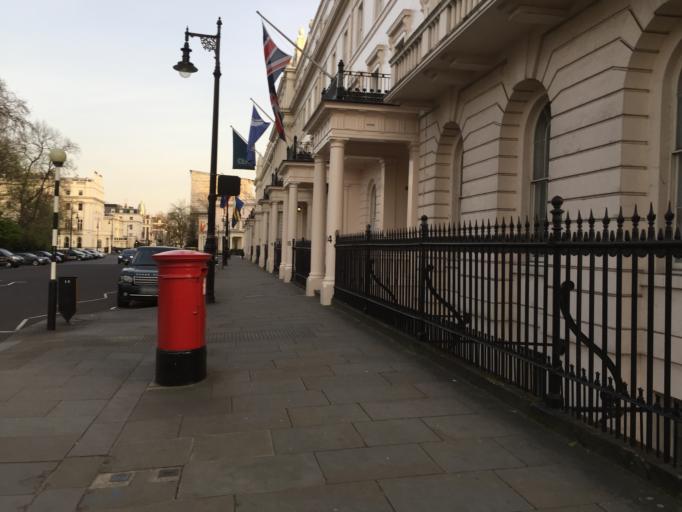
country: GB
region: England
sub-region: Greater London
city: Chelsea
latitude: 51.4990
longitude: -0.1551
